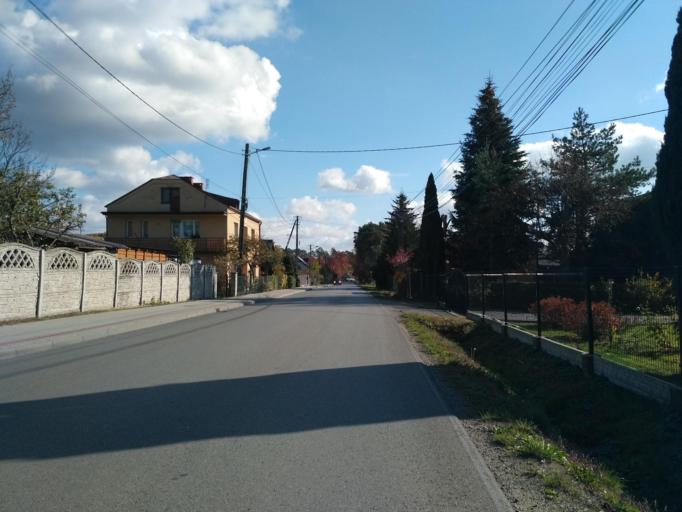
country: PL
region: Subcarpathian Voivodeship
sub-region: Powiat rzeszowski
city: Glogow Malopolski
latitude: 50.1503
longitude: 21.9500
